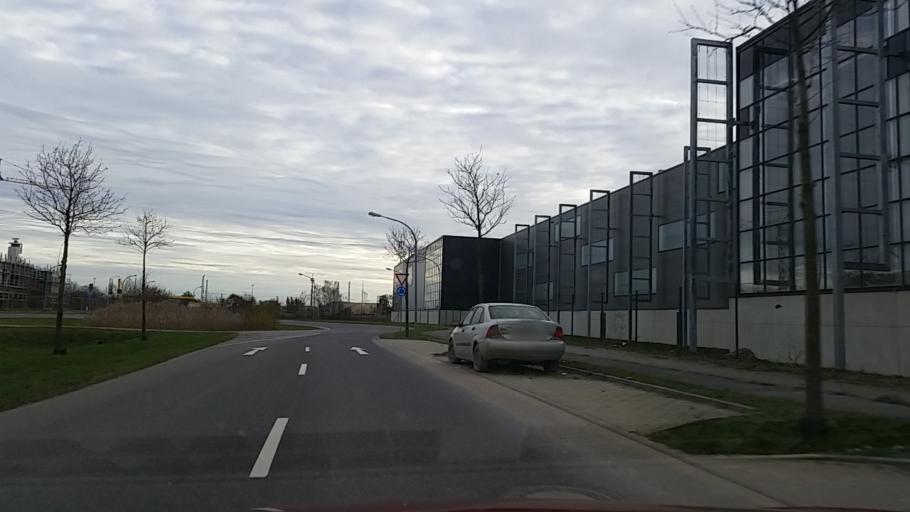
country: DE
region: Brandenburg
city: Schonefeld
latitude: 52.3874
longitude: 13.4988
